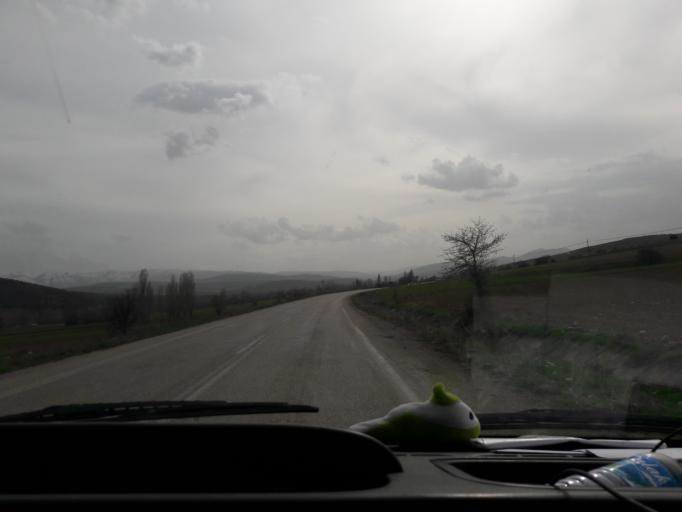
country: TR
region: Gumushane
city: Siran
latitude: 40.1730
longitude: 39.0822
